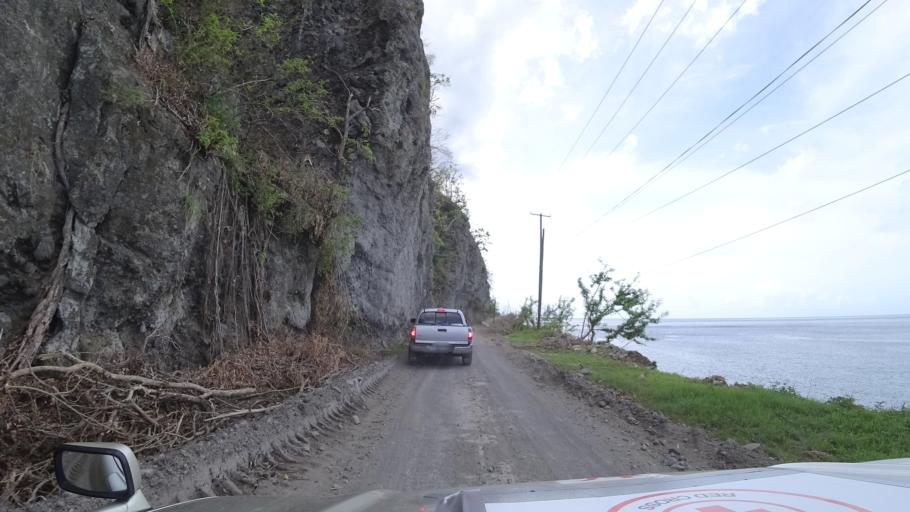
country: DM
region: Saint Luke
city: Pointe Michel
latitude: 15.2548
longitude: -61.3756
